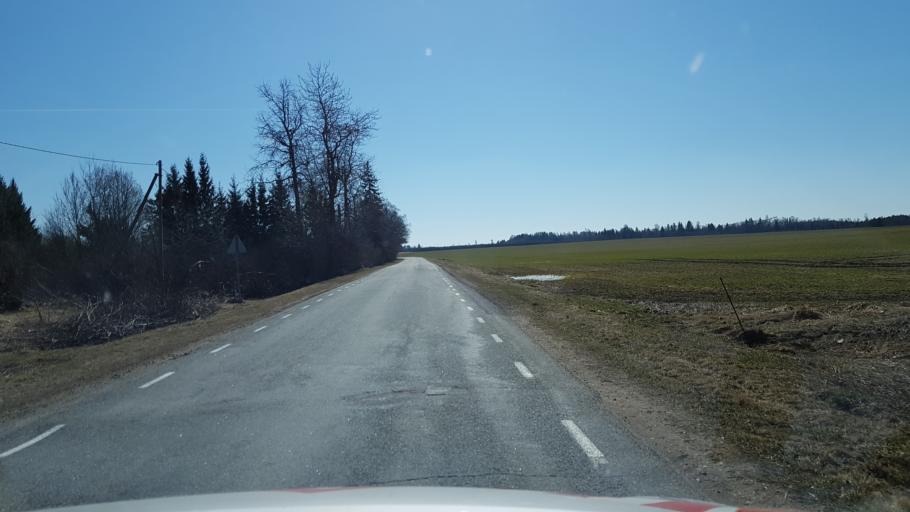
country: EE
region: Laeaene-Virumaa
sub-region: Rakke vald
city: Rakke
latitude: 59.0354
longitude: 26.3473
